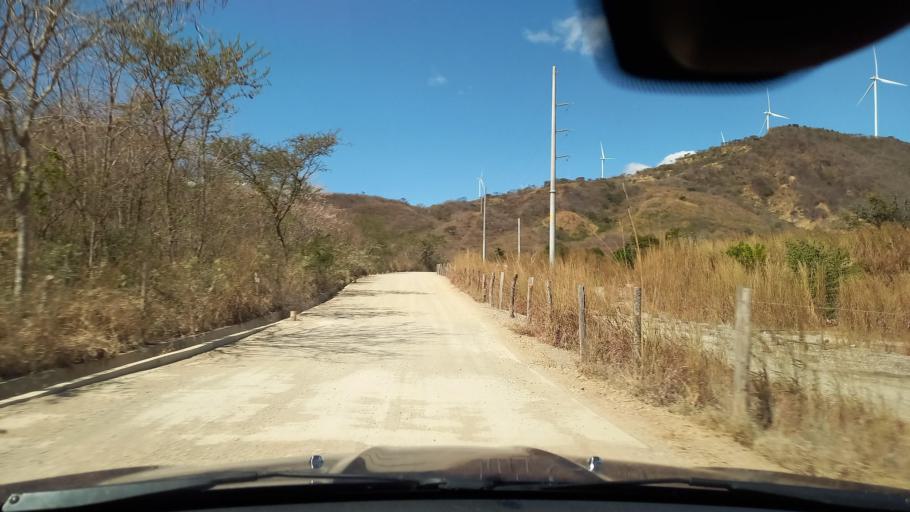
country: SV
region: Santa Ana
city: Metapan
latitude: 14.3601
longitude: -89.4730
